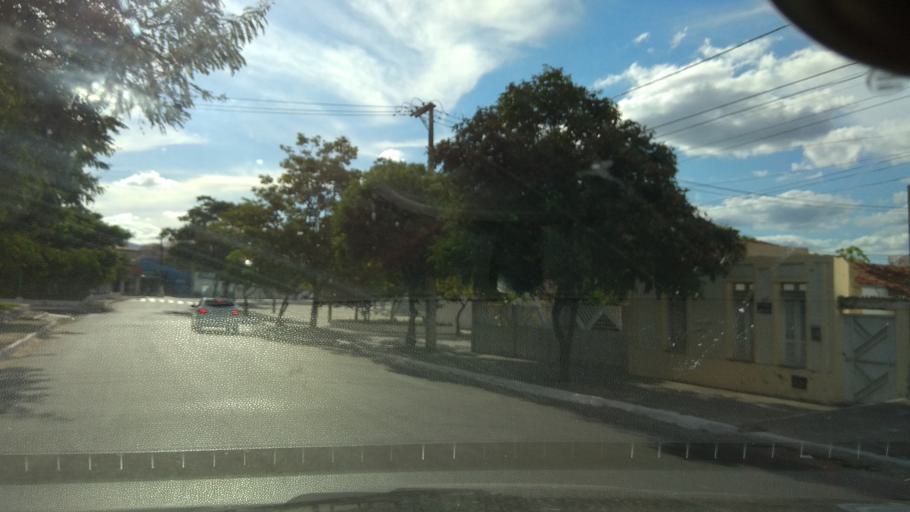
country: BR
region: Bahia
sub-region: Jequie
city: Jequie
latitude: -13.8681
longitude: -40.0754
